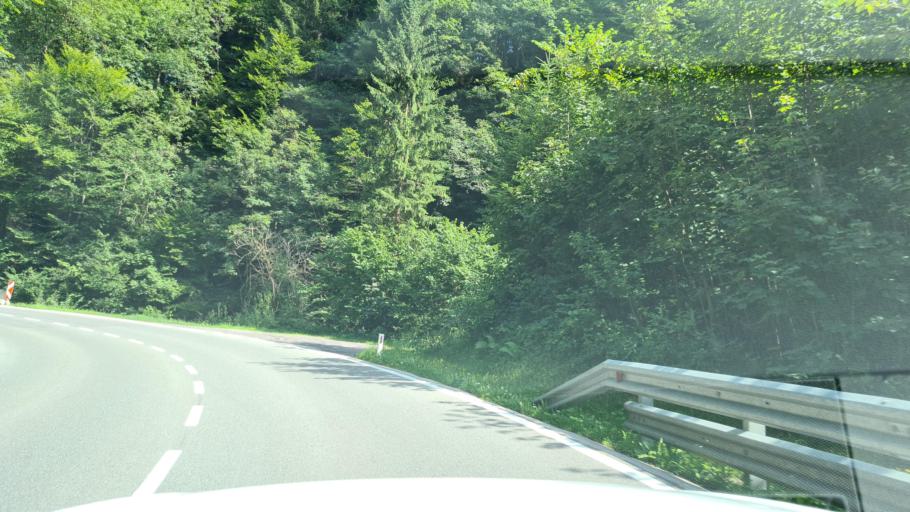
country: AT
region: Vorarlberg
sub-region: Politischer Bezirk Bregenz
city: Bildstein
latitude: 47.4427
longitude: 9.7891
